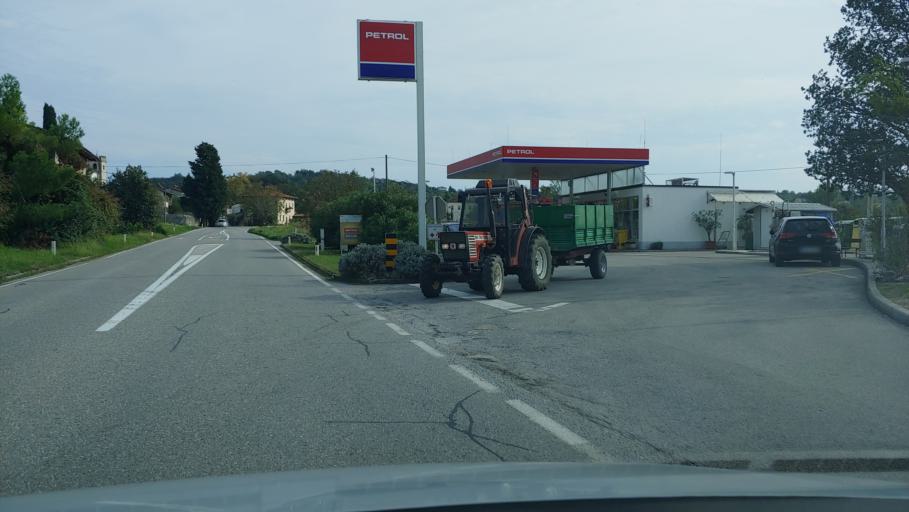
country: SI
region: Nova Gorica
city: Sempas
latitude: 45.9308
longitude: 13.7397
